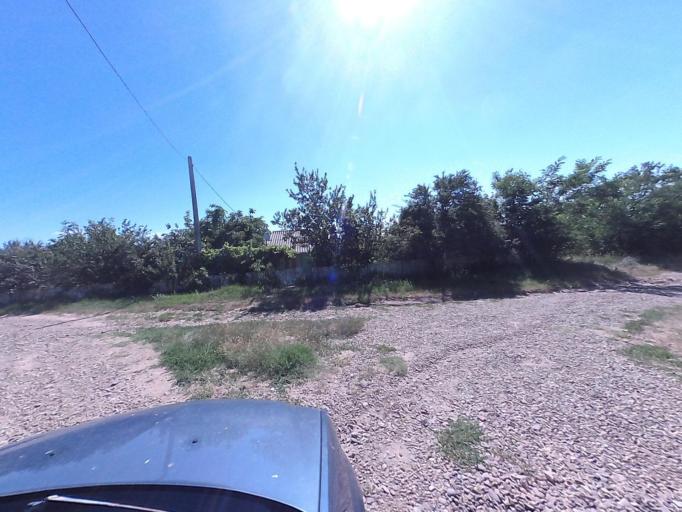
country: RO
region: Vaslui
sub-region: Comuna Costesti
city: Costesti
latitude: 46.4806
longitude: 27.7688
